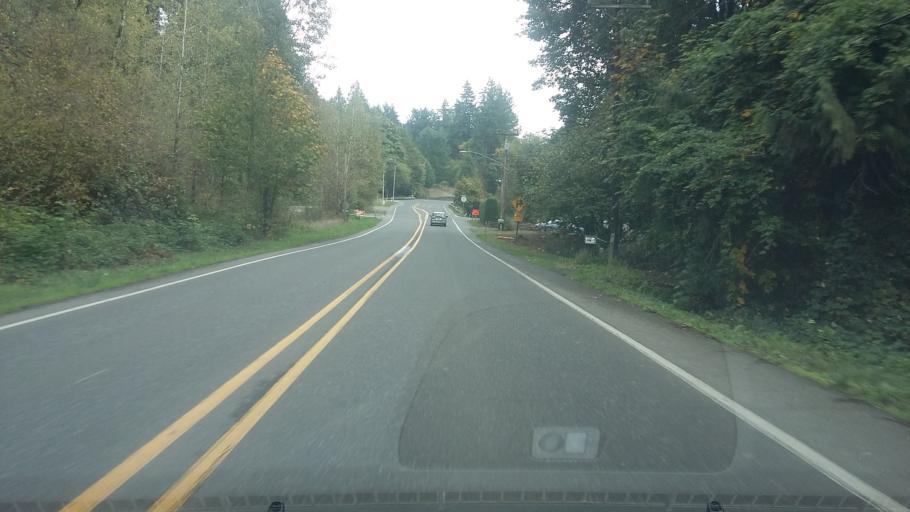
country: US
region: Washington
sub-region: Clark County
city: Ridgefield
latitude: 45.8156
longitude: -122.7287
